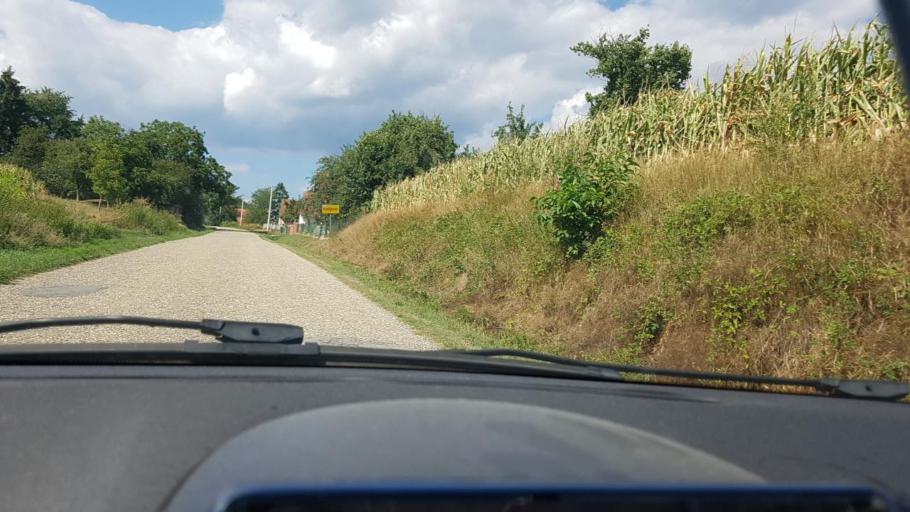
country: HR
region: Bjelovarsko-Bilogorska
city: Zdralovi
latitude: 45.8690
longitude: 17.0010
